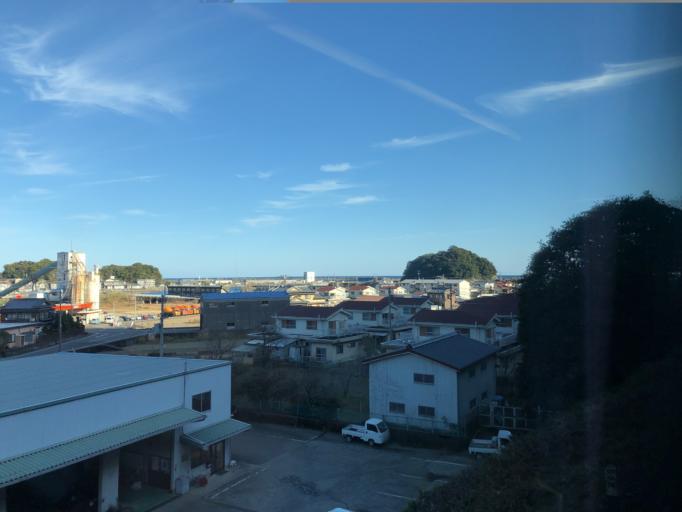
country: JP
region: Kochi
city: Nakamura
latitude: 33.0773
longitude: 133.1033
